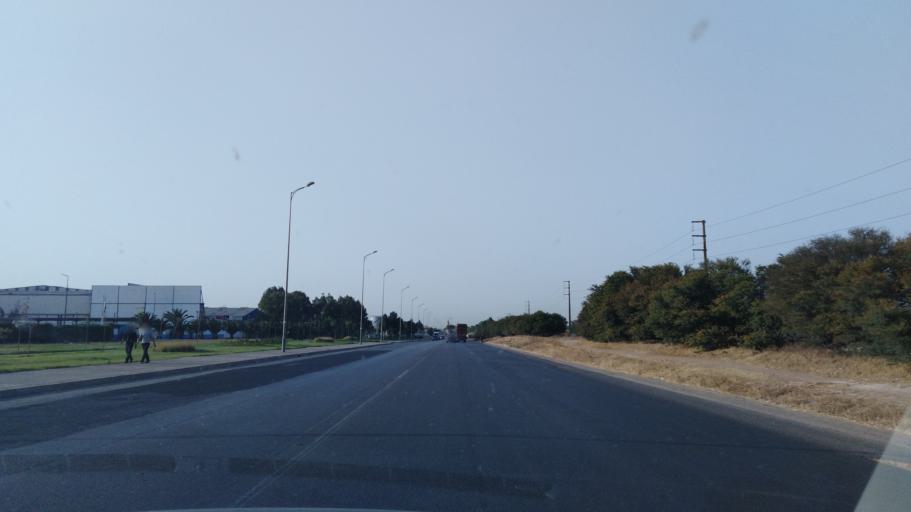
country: MA
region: Chaouia-Ouardigha
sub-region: Settat Province
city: Berrechid
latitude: 33.2488
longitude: -7.5852
